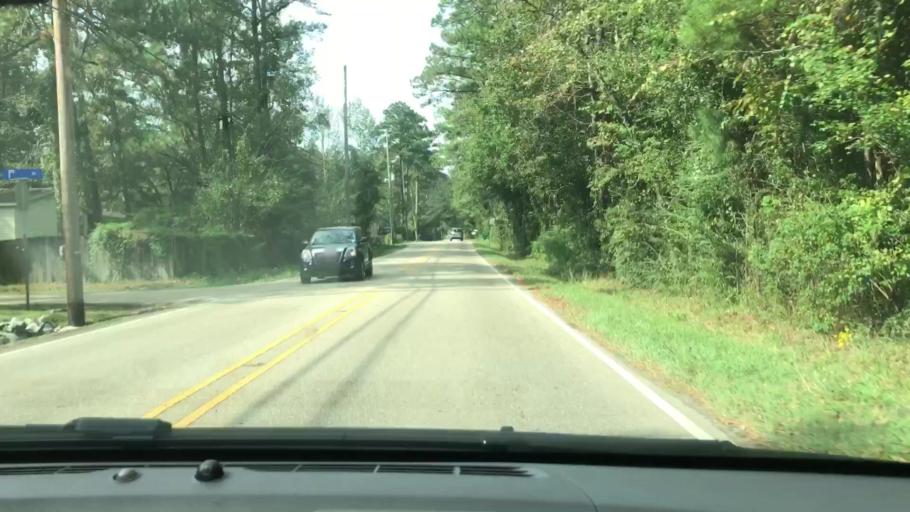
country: US
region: Louisiana
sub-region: Saint Tammany Parish
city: Abita Springs
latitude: 30.4599
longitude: -90.0662
